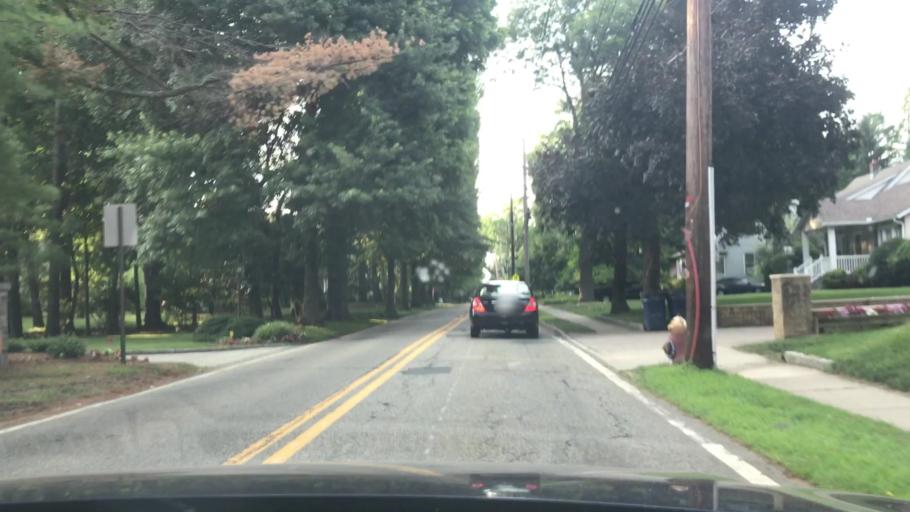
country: US
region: New Jersey
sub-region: Bergen County
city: Norwood
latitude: 40.9905
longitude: -73.9632
